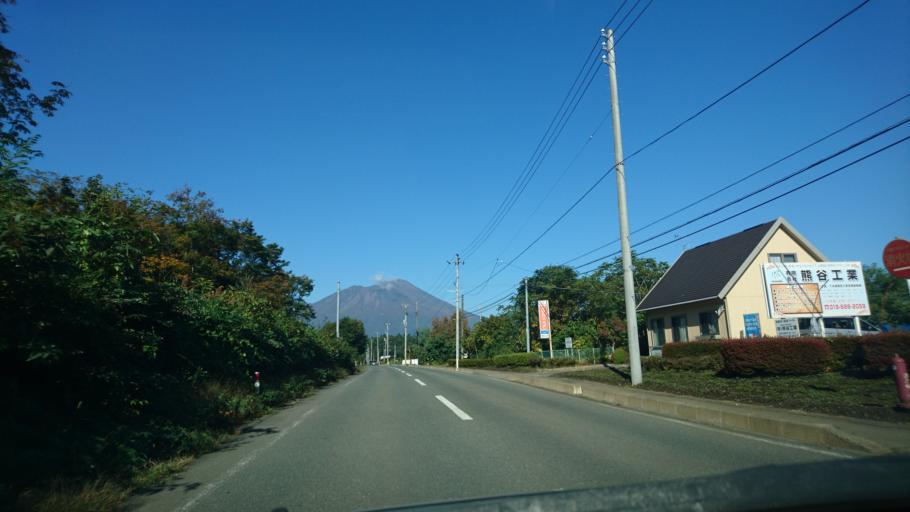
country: JP
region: Iwate
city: Morioka-shi
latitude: 39.8106
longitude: 141.1358
